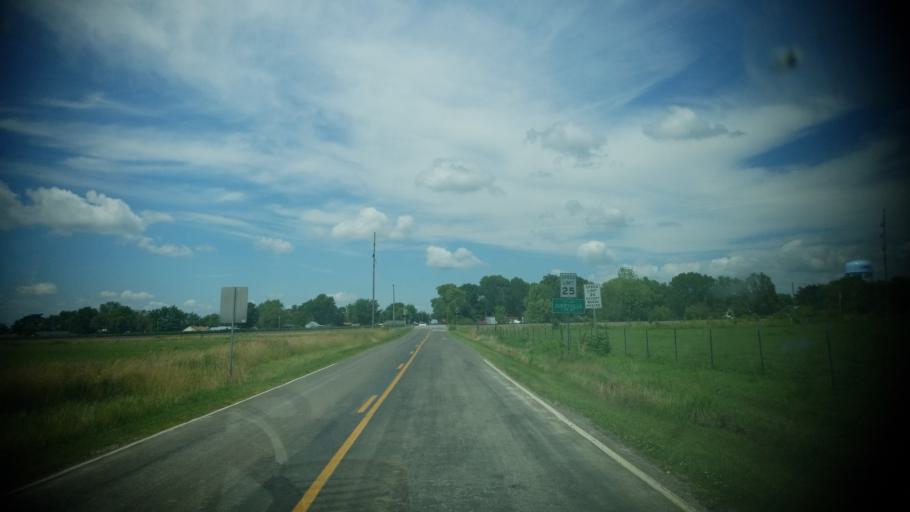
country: US
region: Missouri
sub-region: Audrain County
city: Vandalia
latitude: 39.3414
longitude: -91.3449
